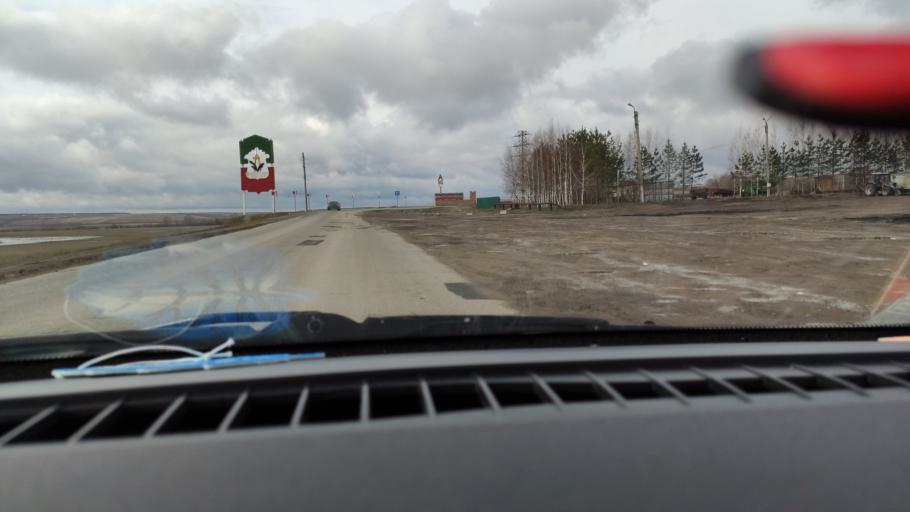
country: RU
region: Tatarstan
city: Cheremshan
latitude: 54.8609
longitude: 51.5948
